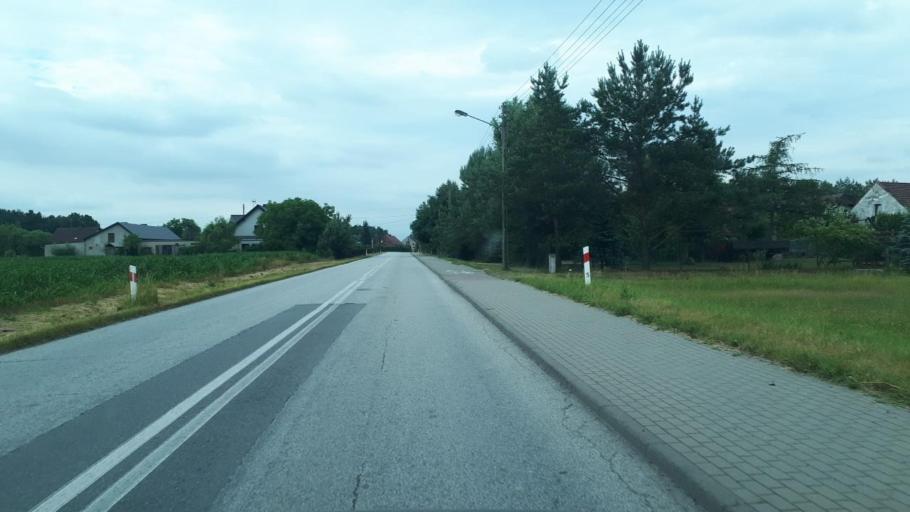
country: PL
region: Opole Voivodeship
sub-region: Powiat strzelecki
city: Zawadzkie
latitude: 50.6674
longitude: 18.4718
